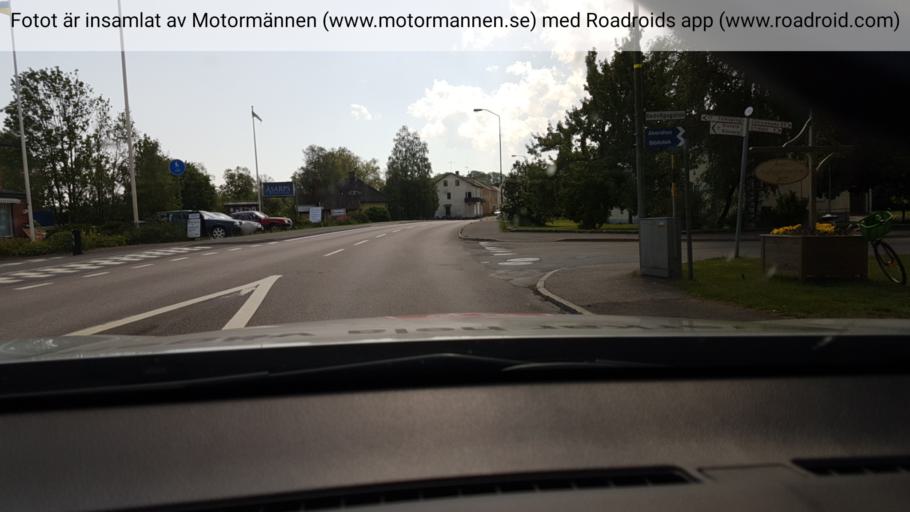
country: SE
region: Vaestra Goetaland
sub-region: Falkopings Kommun
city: Falkoeping
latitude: 58.0242
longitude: 13.5665
